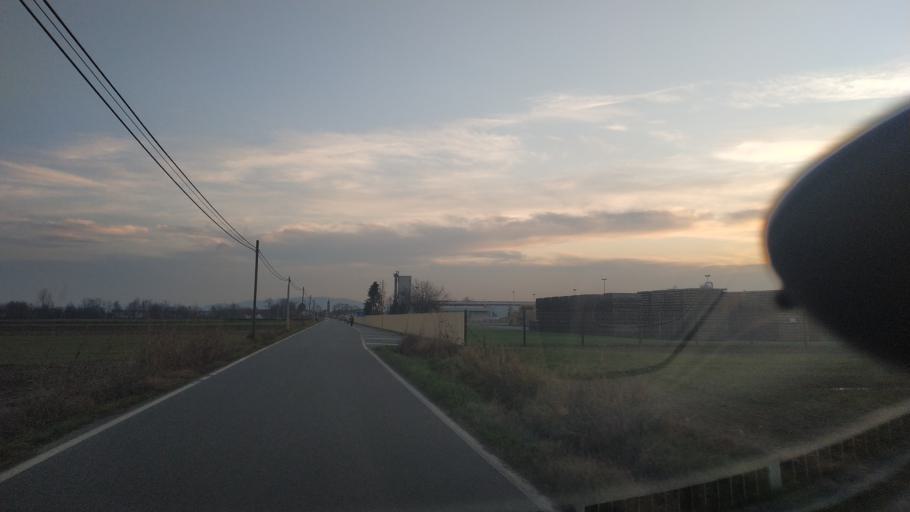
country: IT
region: Piedmont
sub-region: Provincia di Torino
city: Caluso
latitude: 45.2755
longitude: 7.8779
